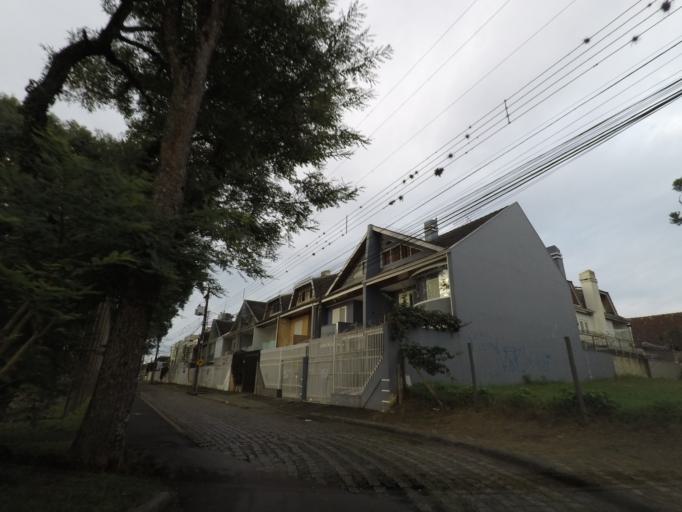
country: BR
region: Parana
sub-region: Curitiba
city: Curitiba
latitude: -25.4241
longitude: -49.2498
